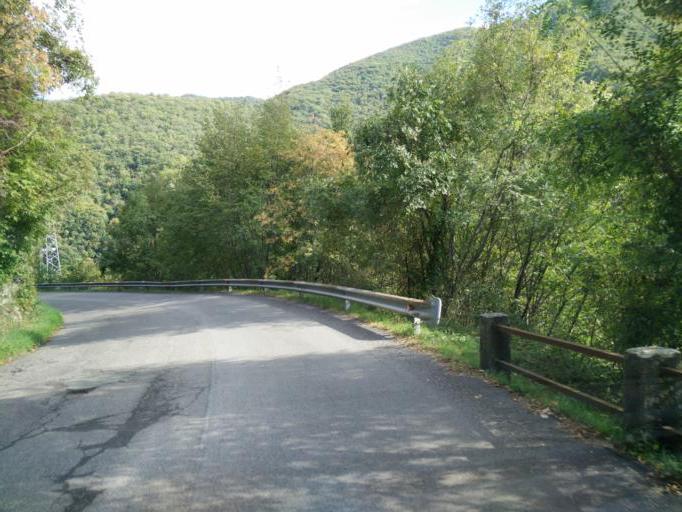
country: IT
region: Tuscany
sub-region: Provincia di Massa-Carrara
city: Zeri
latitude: 44.3518
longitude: 9.8000
